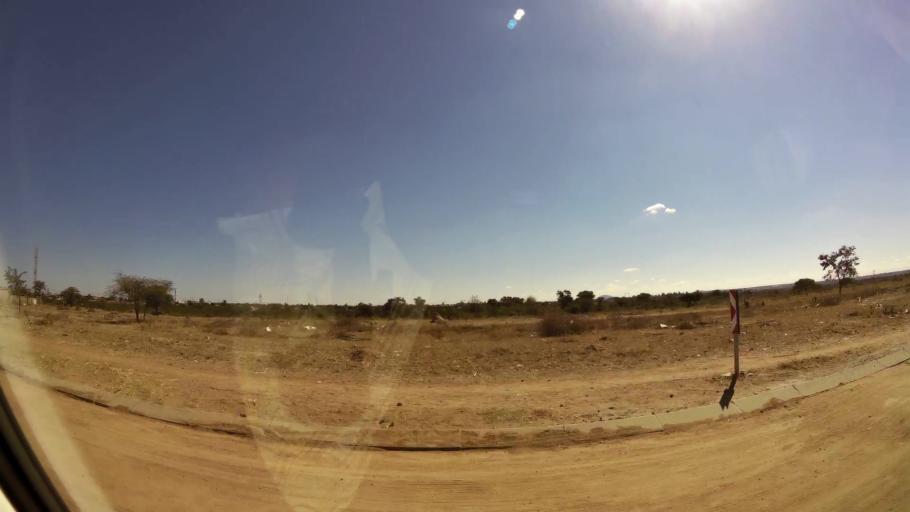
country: ZA
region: Limpopo
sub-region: Capricorn District Municipality
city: Polokwane
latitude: -23.8517
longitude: 29.4094
